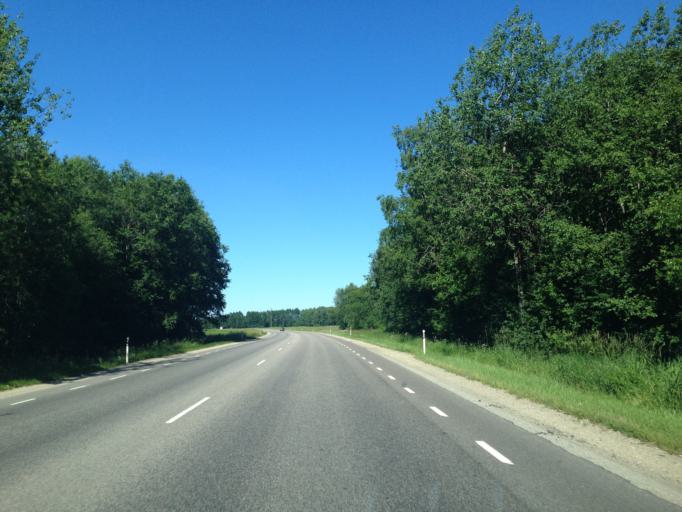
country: EE
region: Harju
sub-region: Rae vald
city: Jueri
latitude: 59.3778
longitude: 24.9154
